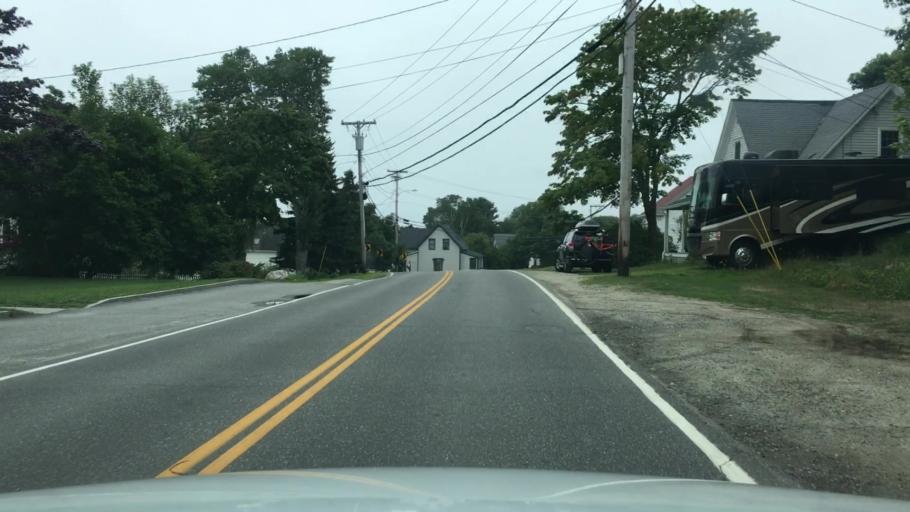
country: US
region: Maine
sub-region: Cumberland County
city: Harpswell Center
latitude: 43.7616
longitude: -69.9762
